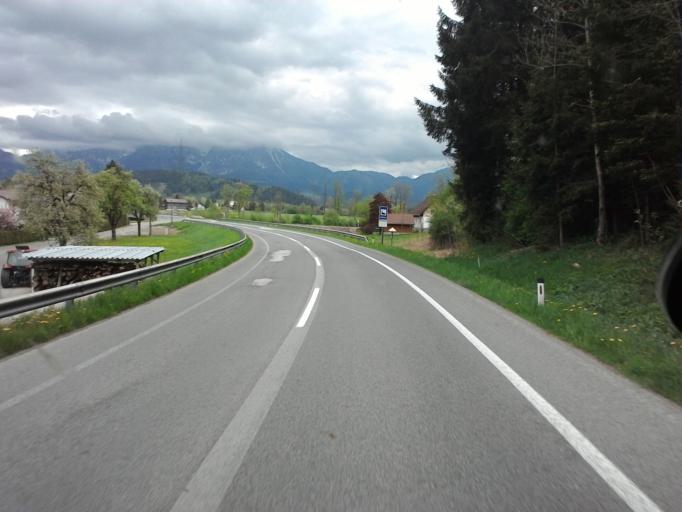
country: AT
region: Upper Austria
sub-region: Politischer Bezirk Kirchdorf an der Krems
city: Rossleithen
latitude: 47.7289
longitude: 14.2936
